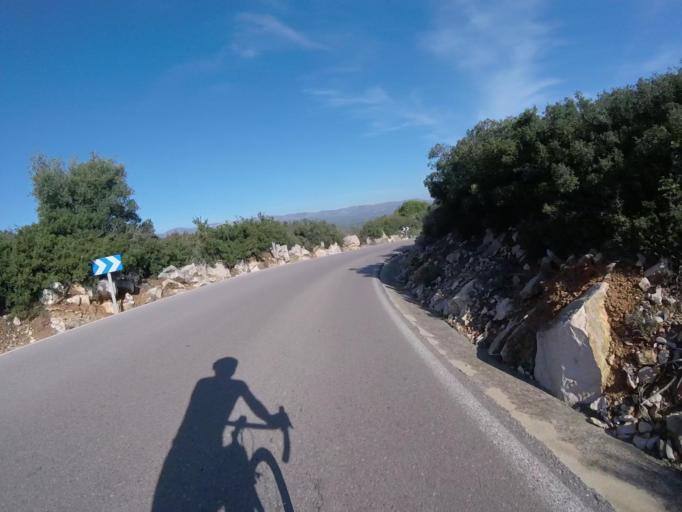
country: ES
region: Valencia
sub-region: Provincia de Castello
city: Benlloch
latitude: 40.2394
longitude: 0.0713
